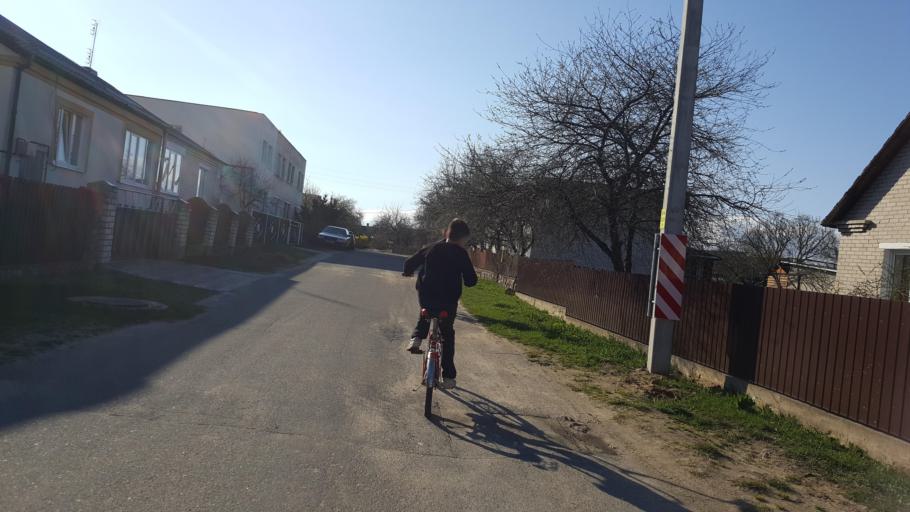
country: BY
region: Brest
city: Kamyanyets
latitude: 52.4020
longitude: 23.8306
